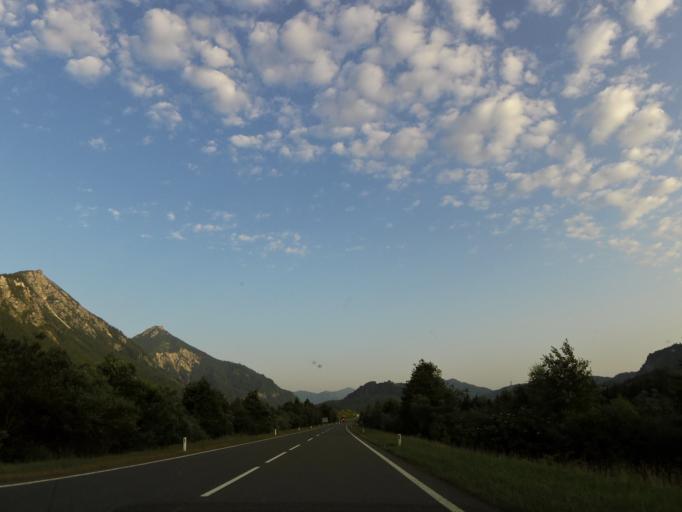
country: AT
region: Tyrol
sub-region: Politischer Bezirk Reutte
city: Pflach
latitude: 47.5270
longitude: 10.6952
